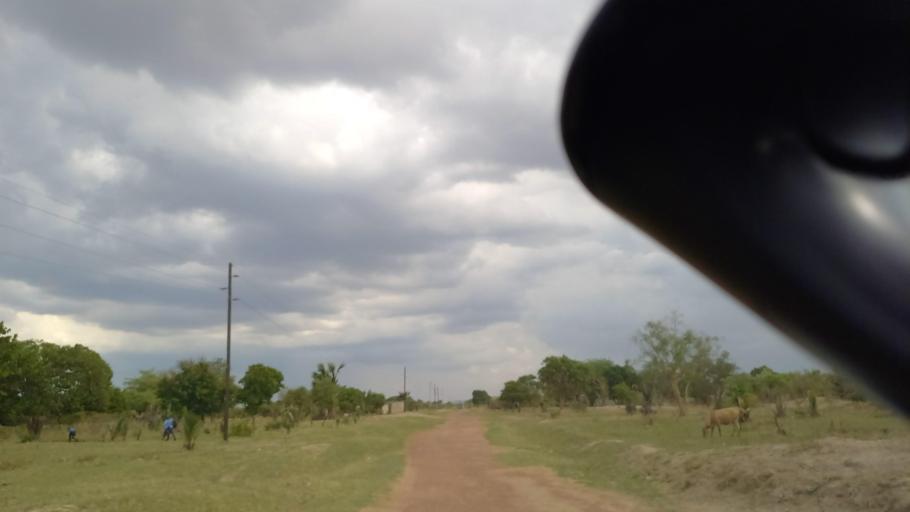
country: ZM
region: Lusaka
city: Kafue
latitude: -15.8485
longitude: 28.1060
